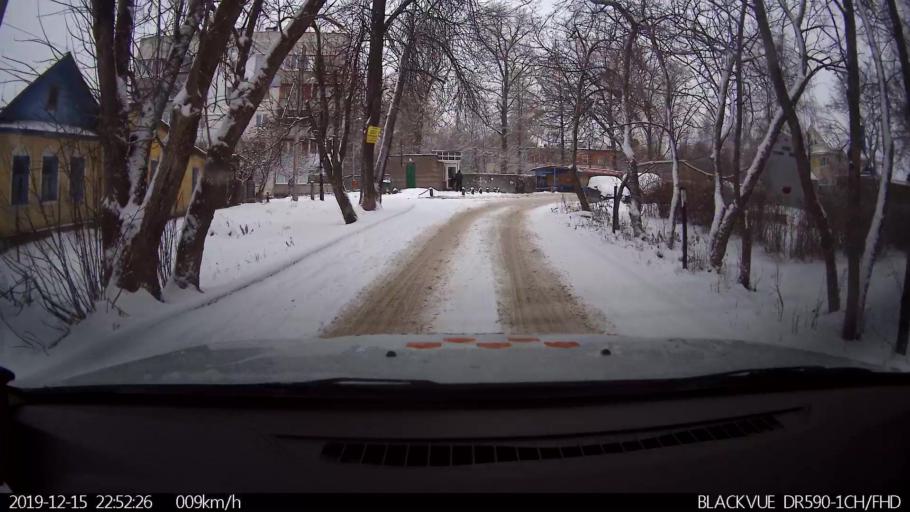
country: RU
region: Nizjnij Novgorod
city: Nizhniy Novgorod
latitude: 56.2337
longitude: 43.9790
